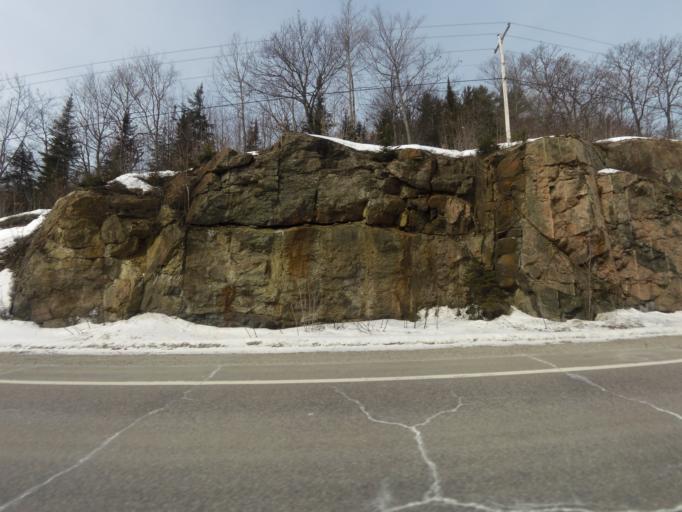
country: CA
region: Quebec
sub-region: Laurentides
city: Mont-Laurier
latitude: 46.3243
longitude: -75.5467
